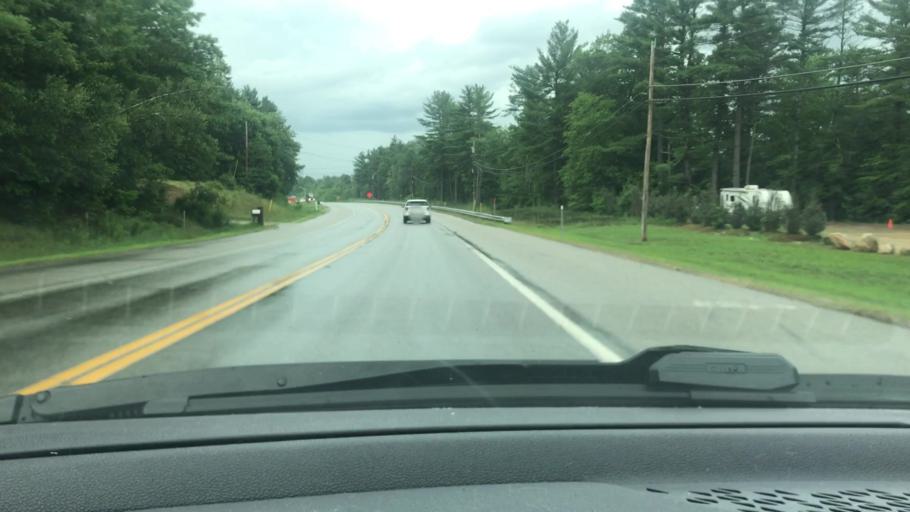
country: US
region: New Hampshire
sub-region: Merrimack County
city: Chichester
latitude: 43.2633
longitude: -71.4575
